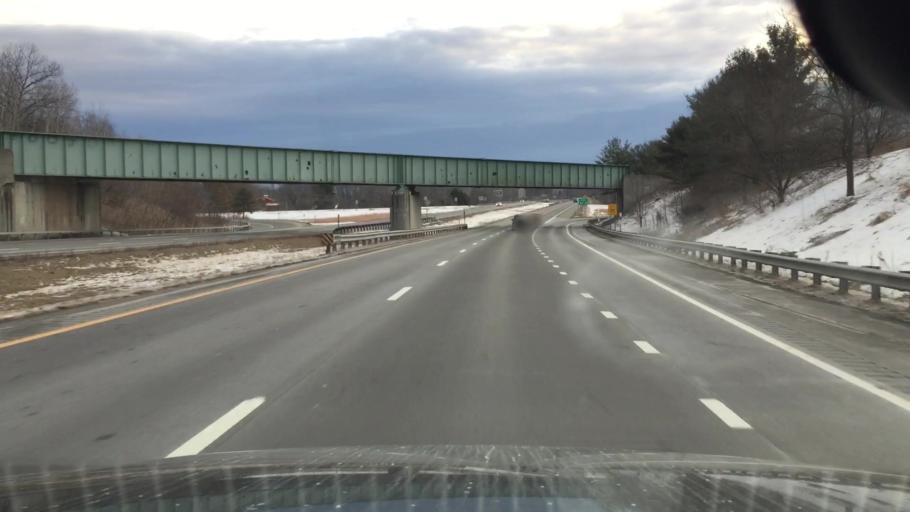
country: US
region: Pennsylvania
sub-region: Bradford County
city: South Waverly
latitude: 42.0000
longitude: -76.5306
